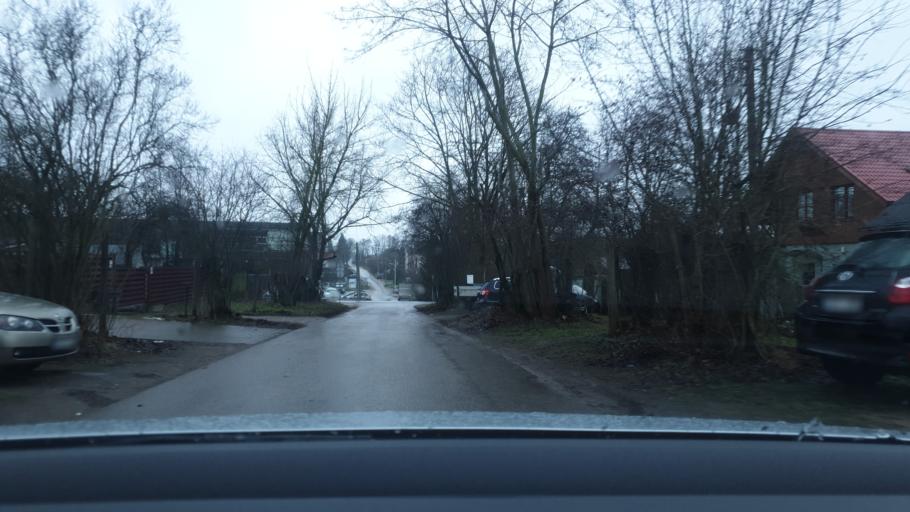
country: LT
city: Skaidiskes
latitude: 54.7019
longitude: 25.4094
